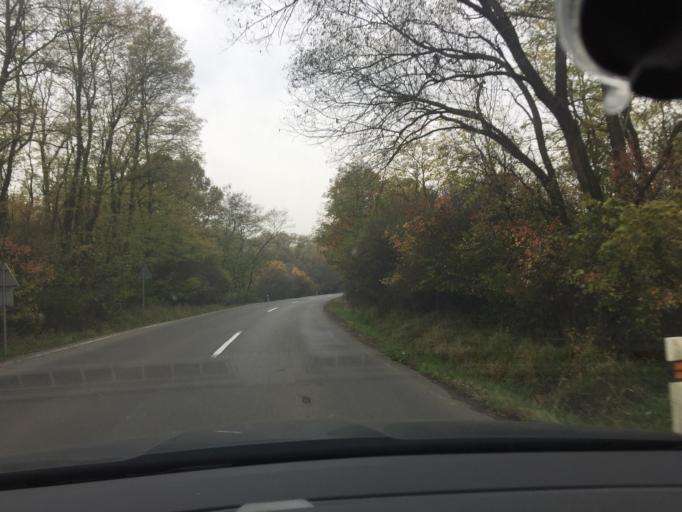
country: SK
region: Banskobystricky
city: Velky Krtis
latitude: 48.2656
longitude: 19.4439
